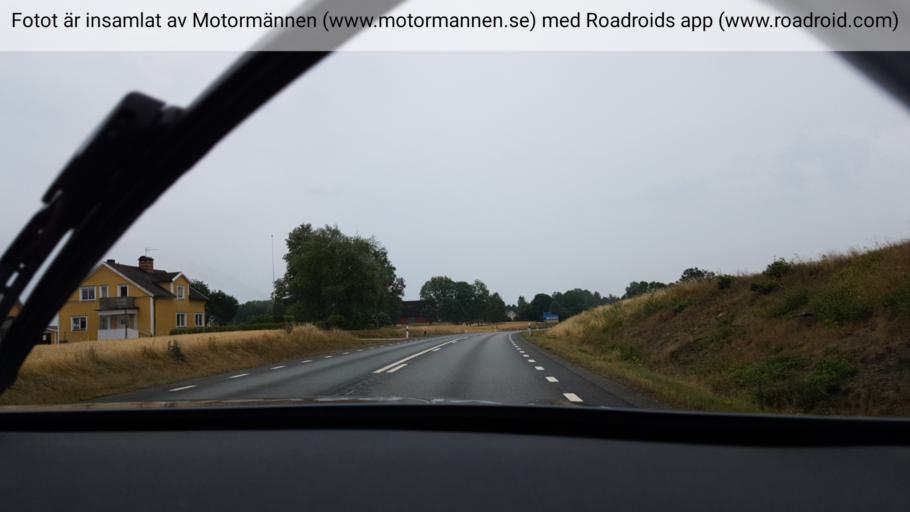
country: SE
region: Joenkoeping
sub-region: Varnamo Kommun
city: Varnamo
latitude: 57.2071
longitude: 14.1018
